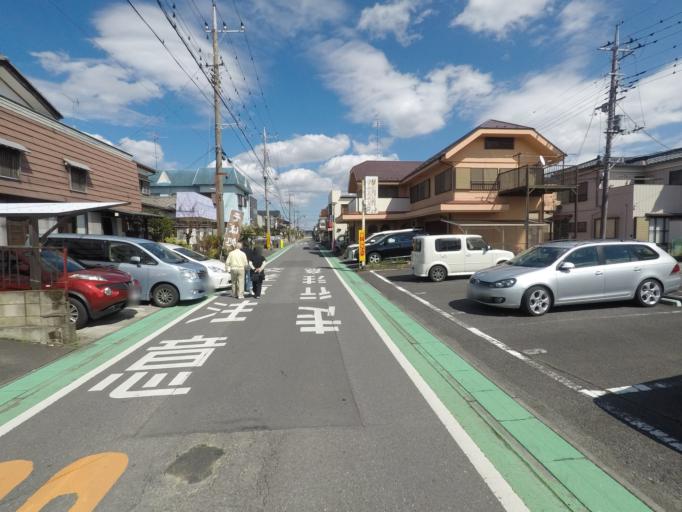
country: JP
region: Ibaraki
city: Fujishiro
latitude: 35.9368
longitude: 140.1221
